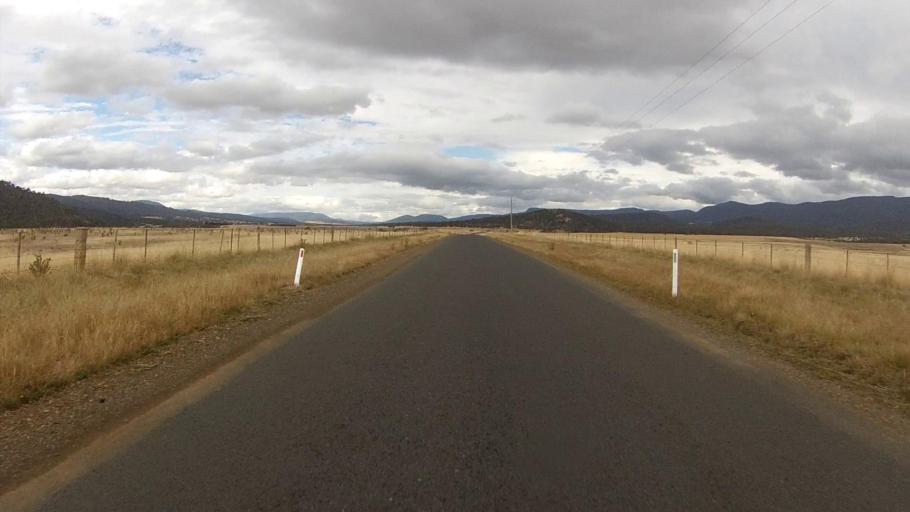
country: AU
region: Tasmania
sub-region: Northern Midlands
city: Evandale
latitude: -41.8256
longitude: 147.7678
